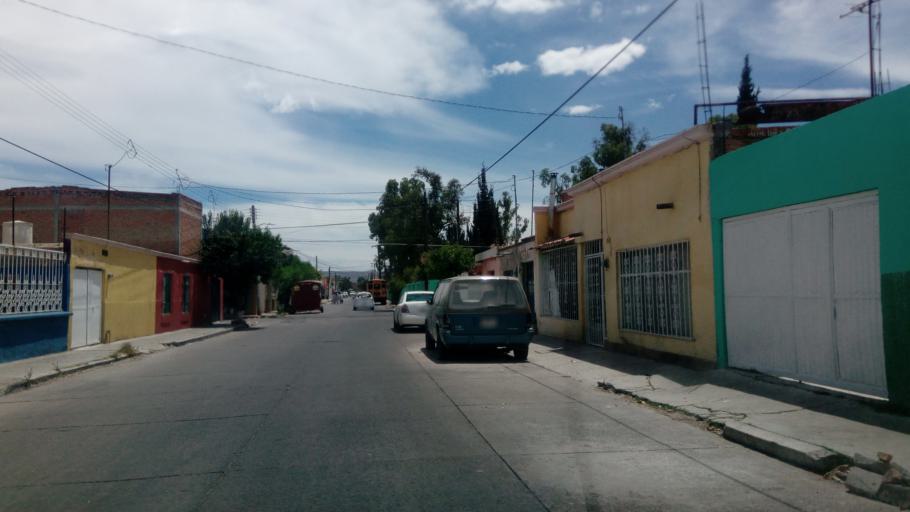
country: MX
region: Durango
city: Victoria de Durango
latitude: 24.0056
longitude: -104.6769
